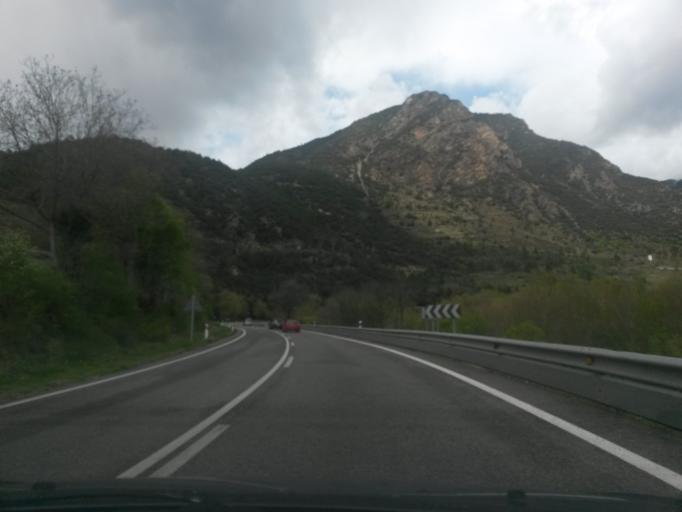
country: ES
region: Catalonia
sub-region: Provincia de Lleida
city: el Pont de Bar
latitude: 42.3637
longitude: 1.5882
